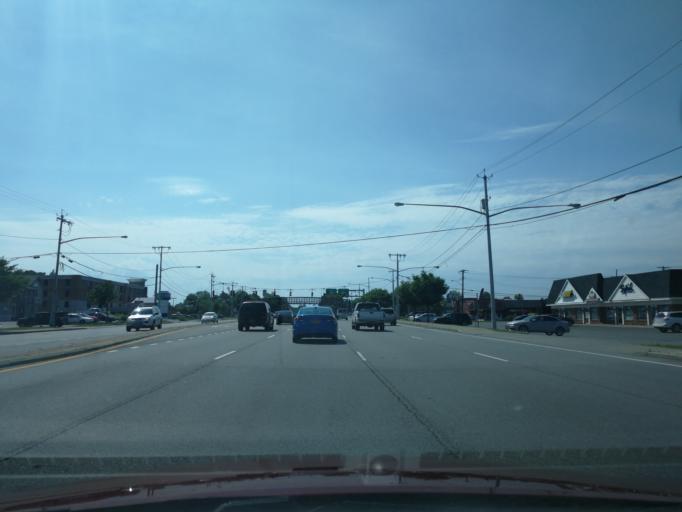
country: US
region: New York
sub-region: Monroe County
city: Greece
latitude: 43.2057
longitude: -77.6689
